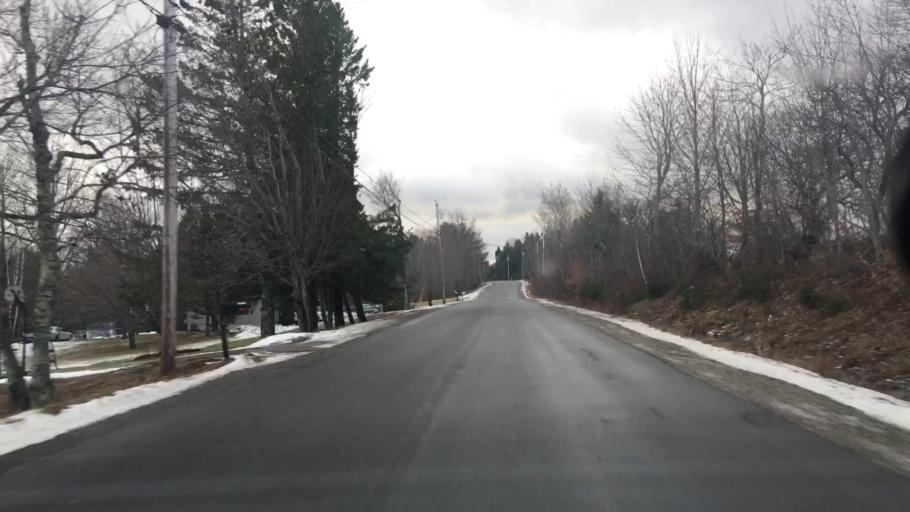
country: US
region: Maine
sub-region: Hancock County
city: Dedham
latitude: 44.6624
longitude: -68.7038
